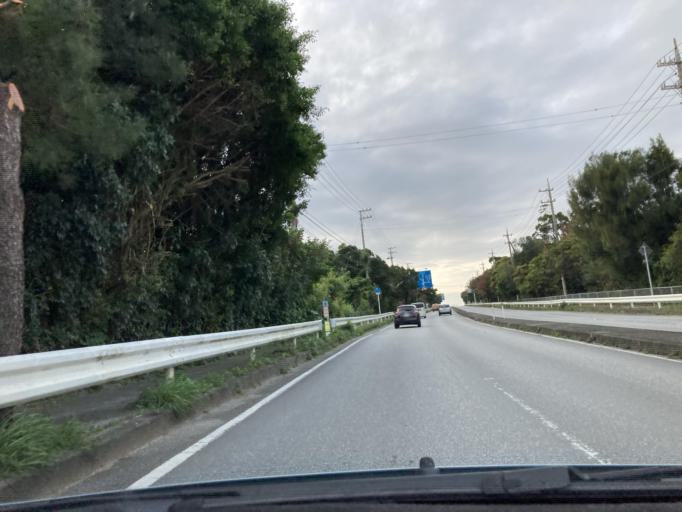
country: JP
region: Okinawa
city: Ishikawa
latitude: 26.4343
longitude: 127.8128
